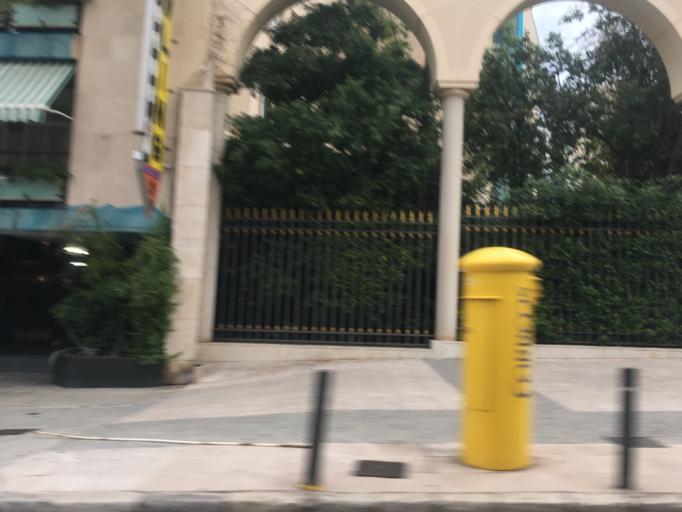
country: ES
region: Balearic Islands
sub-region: Illes Balears
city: Palma
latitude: 39.5642
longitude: 2.6262
